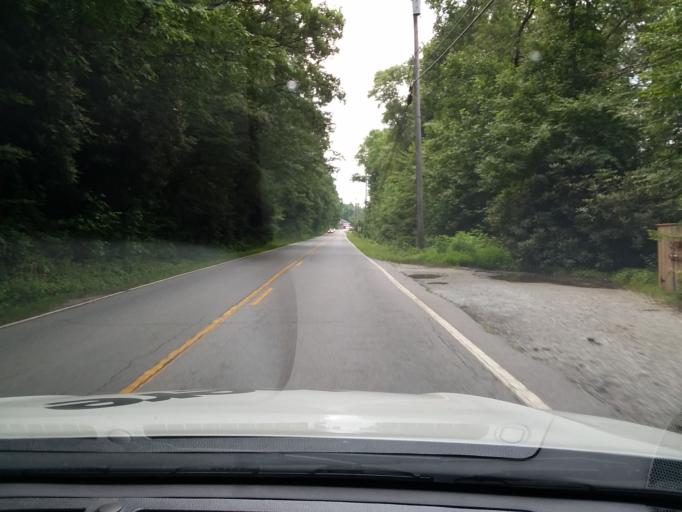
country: US
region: Georgia
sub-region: Rabun County
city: Mountain City
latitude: 35.0444
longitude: -83.2035
